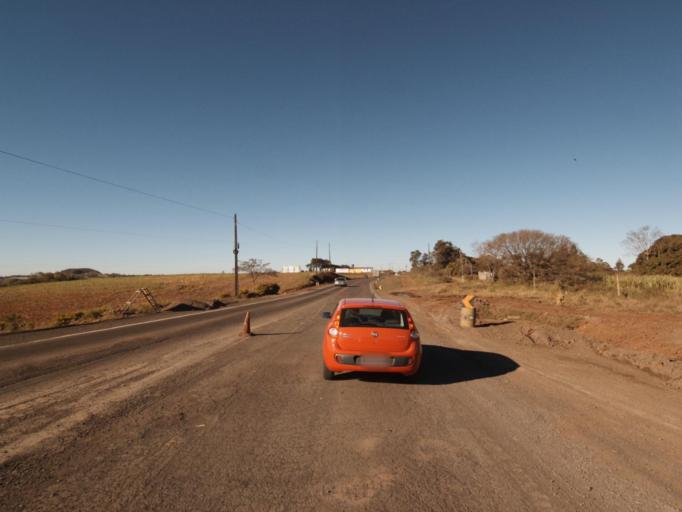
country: AR
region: Misiones
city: Bernardo de Irigoyen
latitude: -26.6396
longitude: -53.5184
